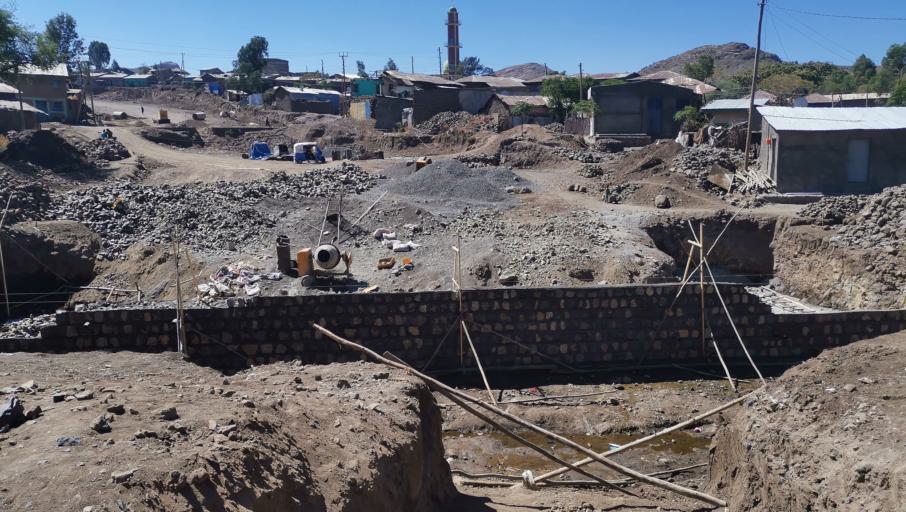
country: ET
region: Tigray
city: Korem
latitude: 12.6313
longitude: 39.0365
